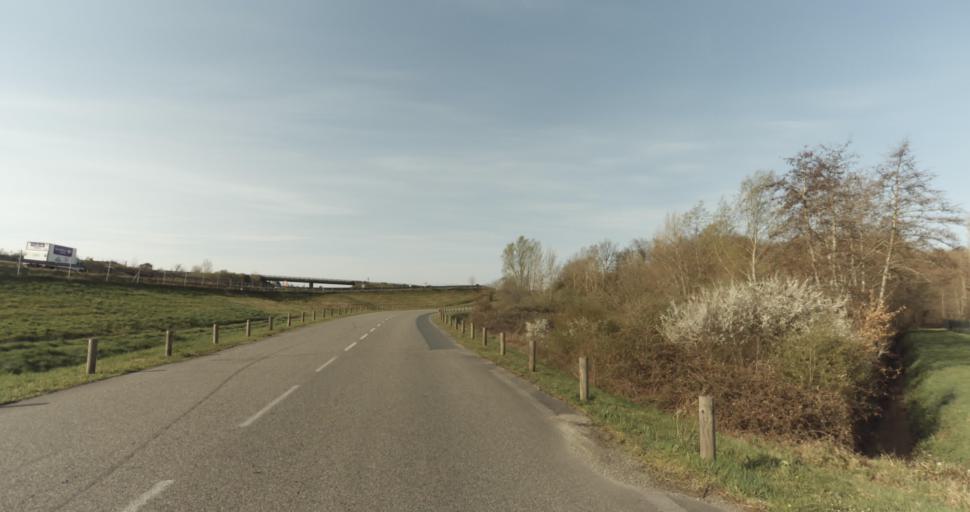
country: FR
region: Midi-Pyrenees
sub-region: Departement du Tarn
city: Saint-Sulpice-la-Pointe
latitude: 43.7607
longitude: 1.7120
